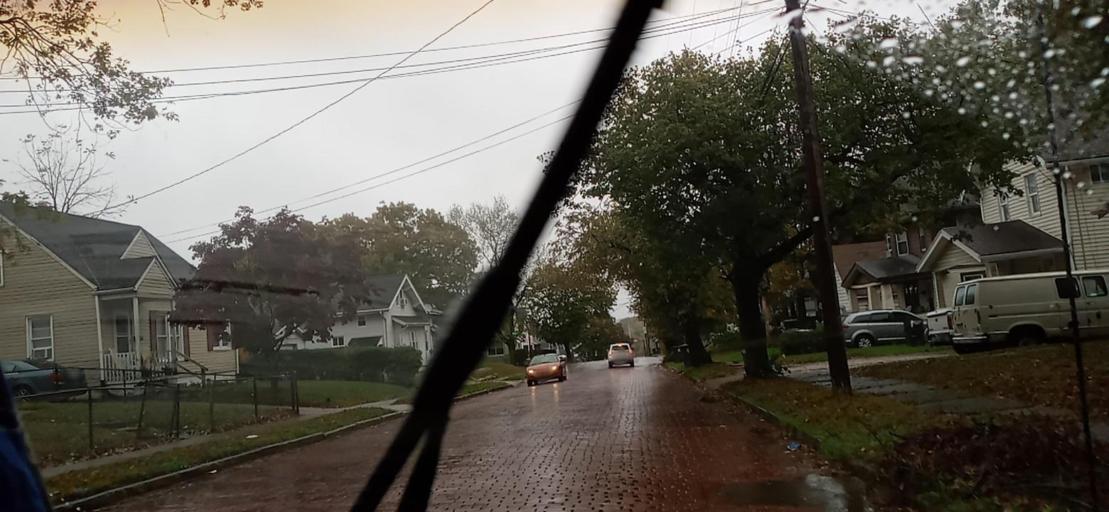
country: US
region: Ohio
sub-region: Summit County
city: Akron
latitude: 41.0615
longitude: -81.5542
